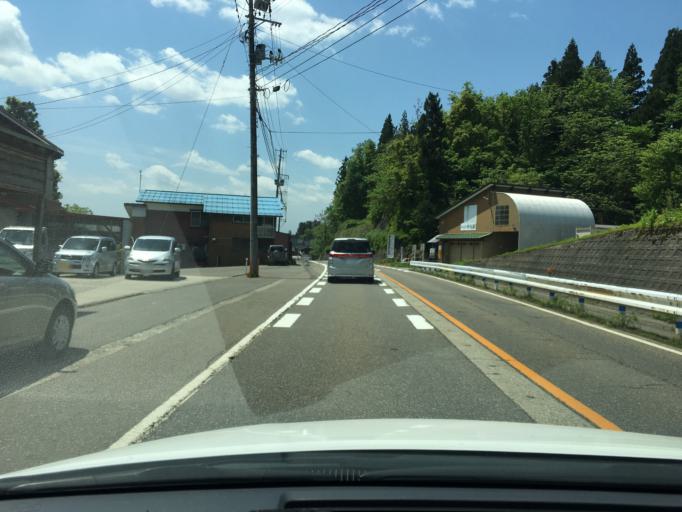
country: JP
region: Niigata
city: Tochio-honcho
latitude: 37.2989
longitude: 138.9943
